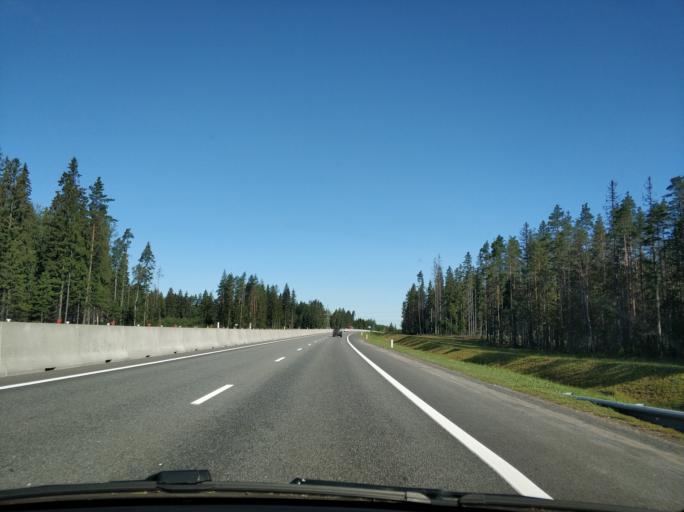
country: RU
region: Leningrad
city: Sosnovo
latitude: 60.5204
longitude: 30.1735
